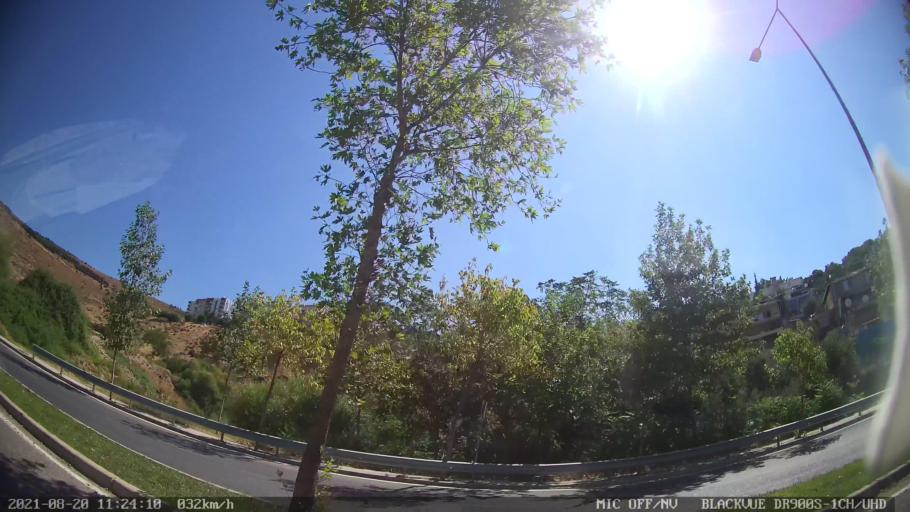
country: TR
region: Izmir
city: Karsiyaka
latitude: 38.5026
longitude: 27.0840
